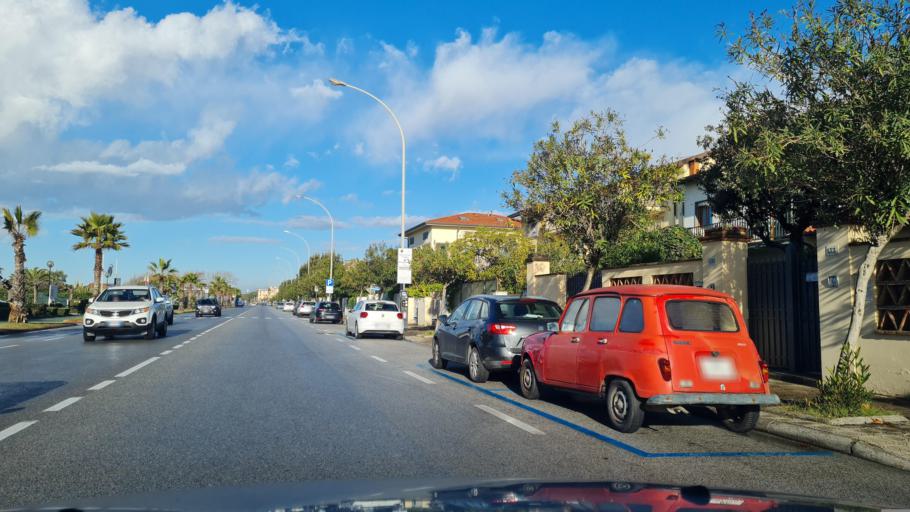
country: IT
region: Tuscany
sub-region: Provincia di Lucca
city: Pietrasanta
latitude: 43.9334
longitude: 10.1934
